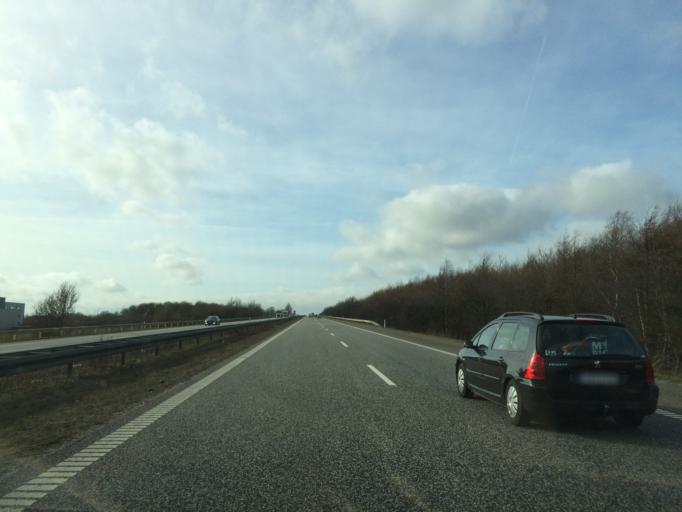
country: DK
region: Central Jutland
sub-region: Randers Kommune
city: Randers
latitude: 56.4281
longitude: 10.0440
